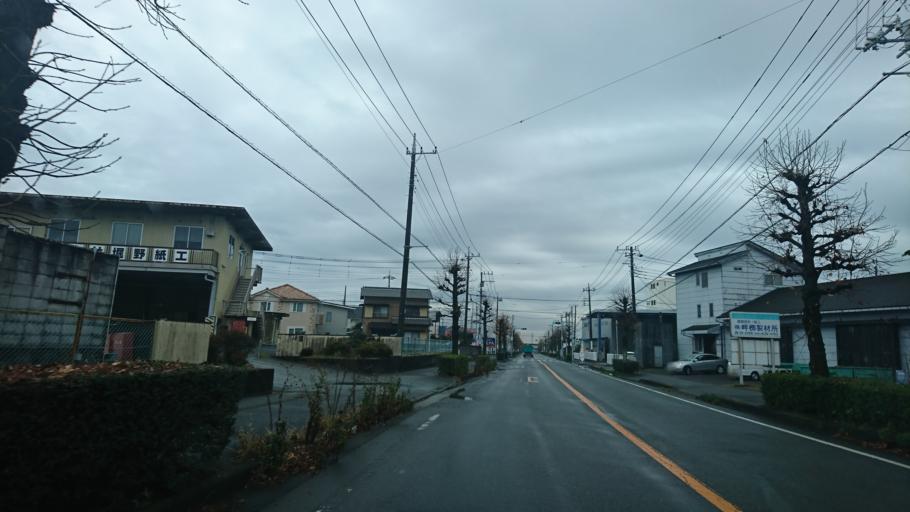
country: JP
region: Shizuoka
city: Fuji
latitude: 35.1580
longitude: 138.7431
